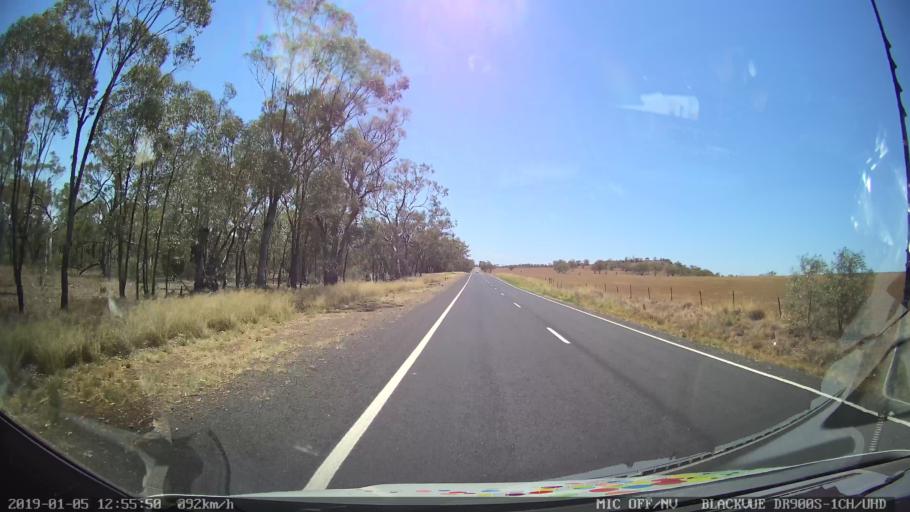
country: AU
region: New South Wales
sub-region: Warrumbungle Shire
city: Coonabarabran
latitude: -31.1189
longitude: 149.7118
